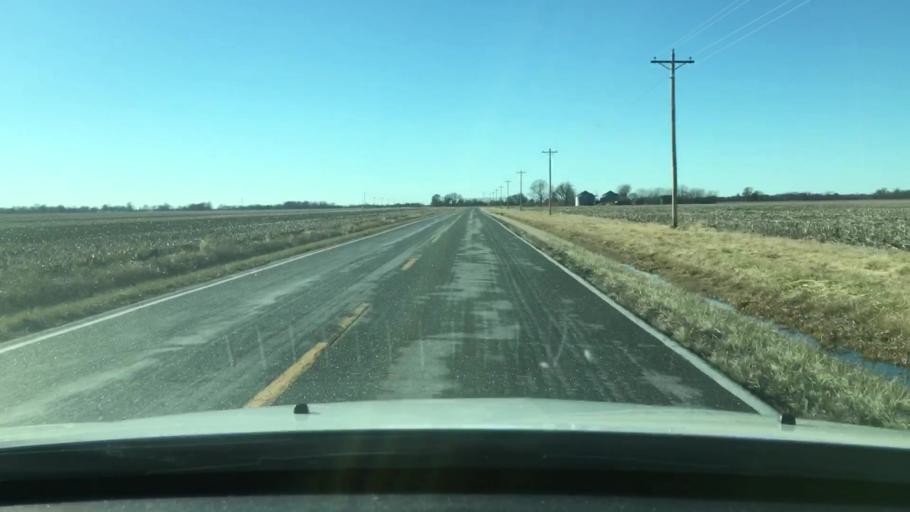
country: US
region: Missouri
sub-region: Audrain County
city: Mexico
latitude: 39.2816
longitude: -91.7318
